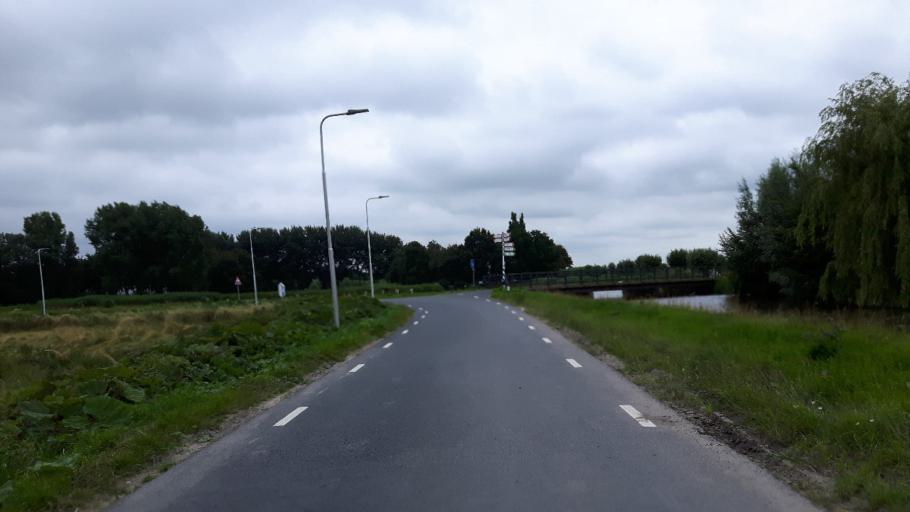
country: NL
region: South Holland
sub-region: Gemeente Pijnacker-Nootdorp
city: Pijnacker
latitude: 51.9795
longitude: 4.4290
